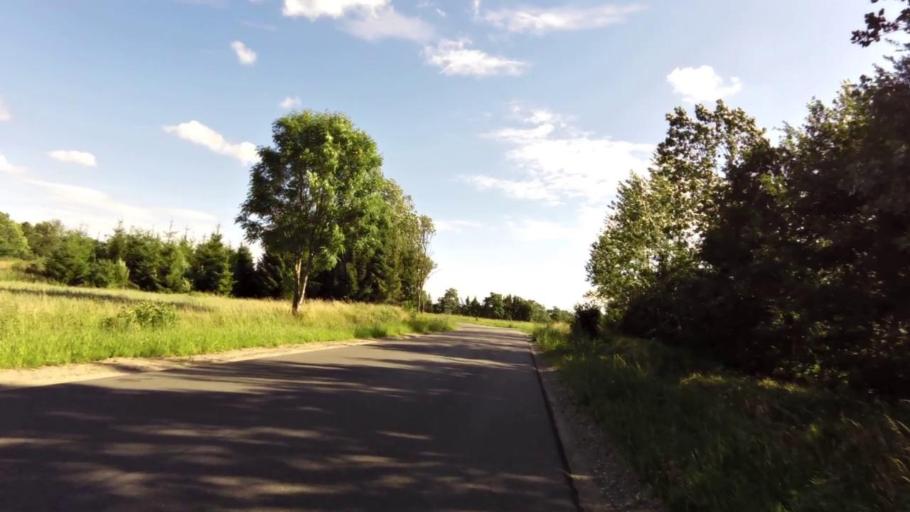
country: PL
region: West Pomeranian Voivodeship
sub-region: Powiat slawienski
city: Slawno
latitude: 54.4374
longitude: 16.7326
